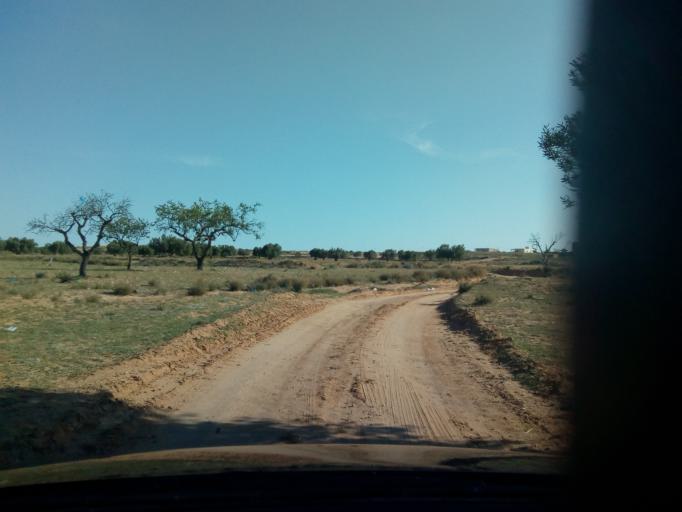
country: TN
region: Safaqis
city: Sfax
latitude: 34.7248
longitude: 10.6127
